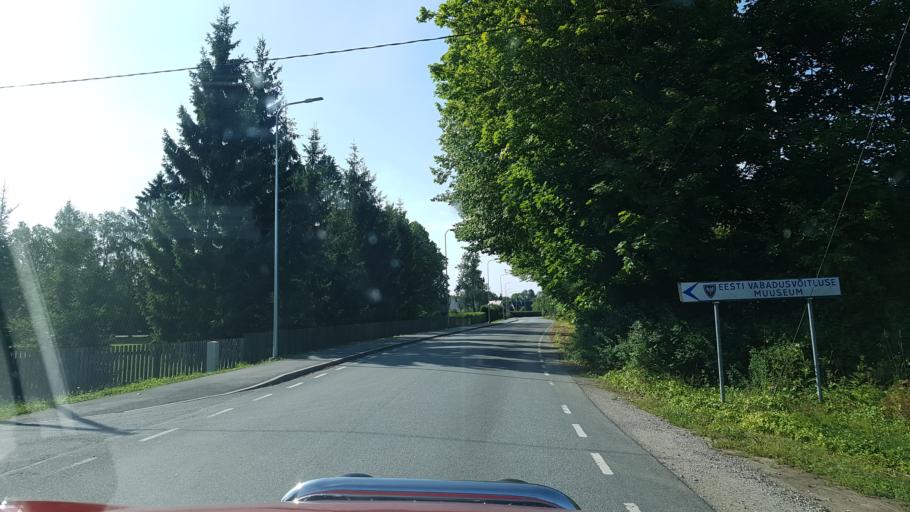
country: EE
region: Harju
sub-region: Joelaehtme vald
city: Loo
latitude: 59.3916
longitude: 24.9343
